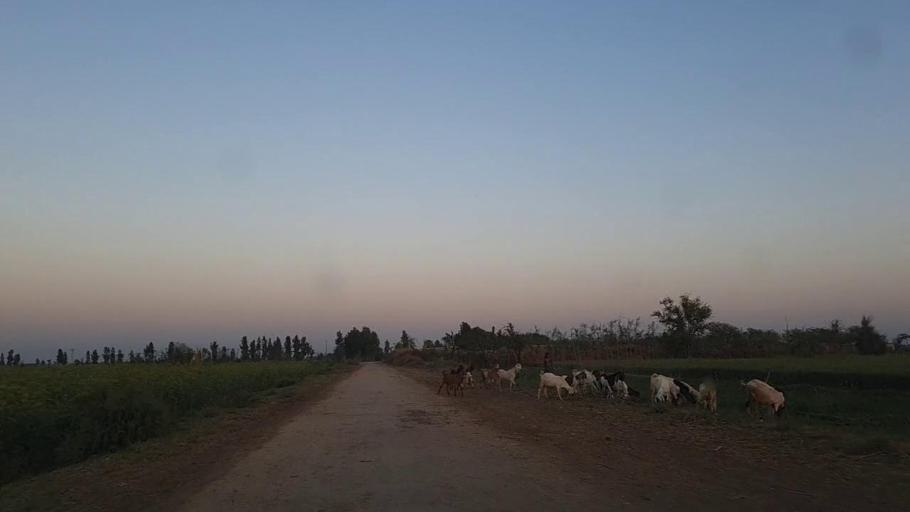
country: PK
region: Sindh
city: Samaro
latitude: 25.3108
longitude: 69.4100
